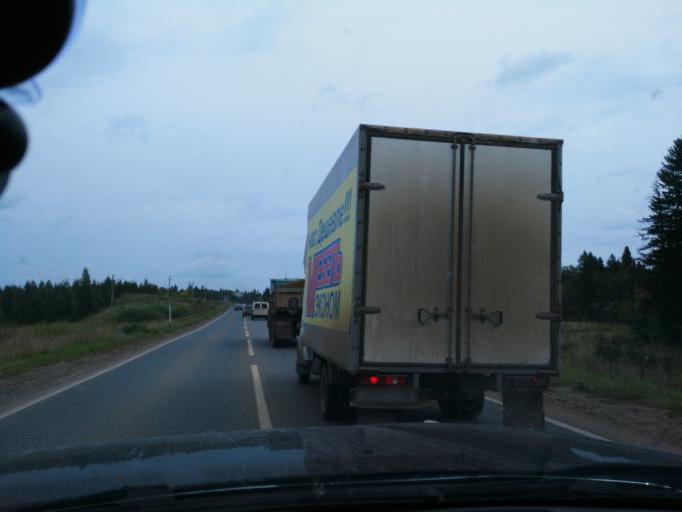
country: RU
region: Perm
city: Chernushka
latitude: 56.5048
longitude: 55.8729
